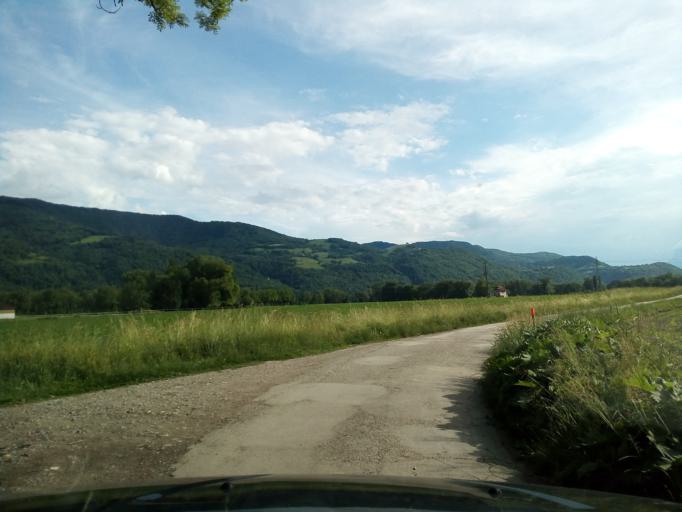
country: FR
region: Rhone-Alpes
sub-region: Departement de l'Isere
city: Domene
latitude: 45.2122
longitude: 5.8233
